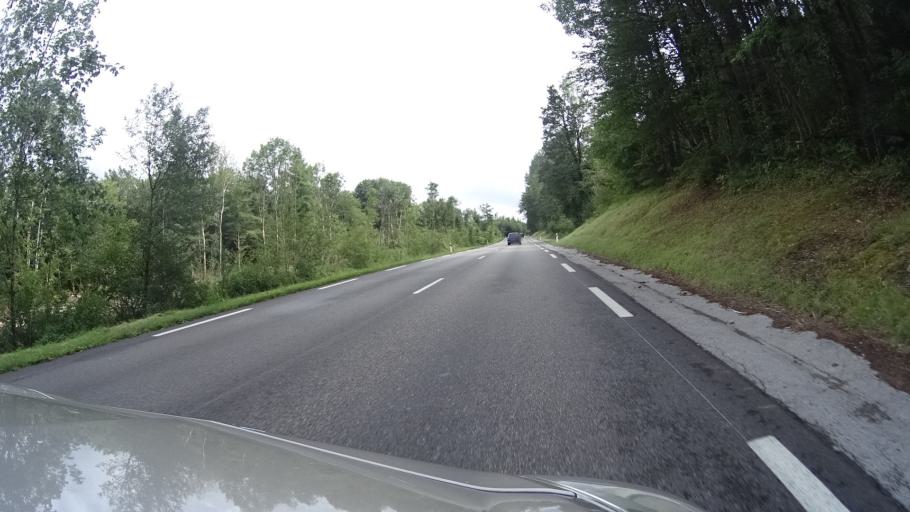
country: FR
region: Franche-Comte
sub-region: Departement du Jura
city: Champagnole
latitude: 46.7142
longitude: 5.9266
